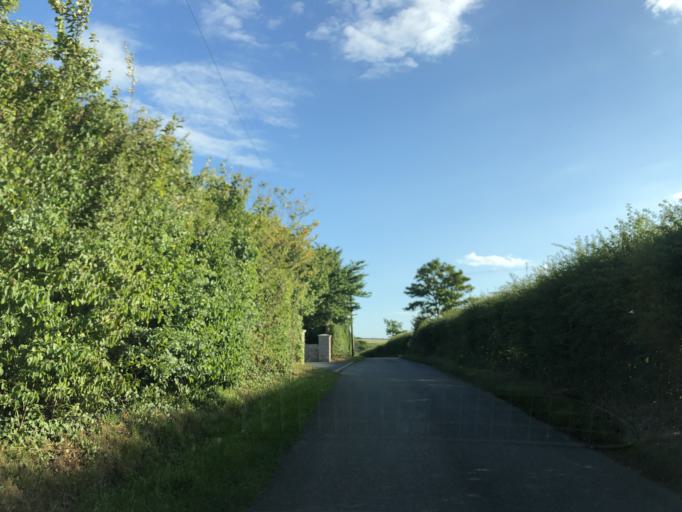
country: GB
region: England
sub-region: Isle of Wight
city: Yarmouth
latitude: 50.7012
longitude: -1.4702
